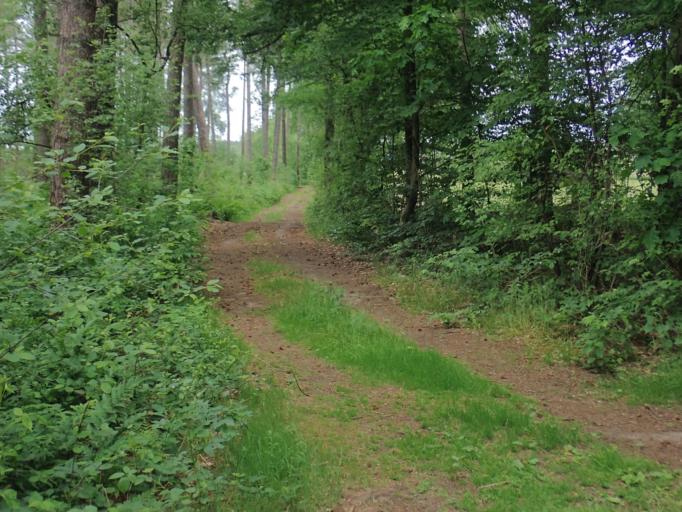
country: BE
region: Flanders
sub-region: Provincie Antwerpen
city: Herentals
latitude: 51.2008
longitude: 4.8139
